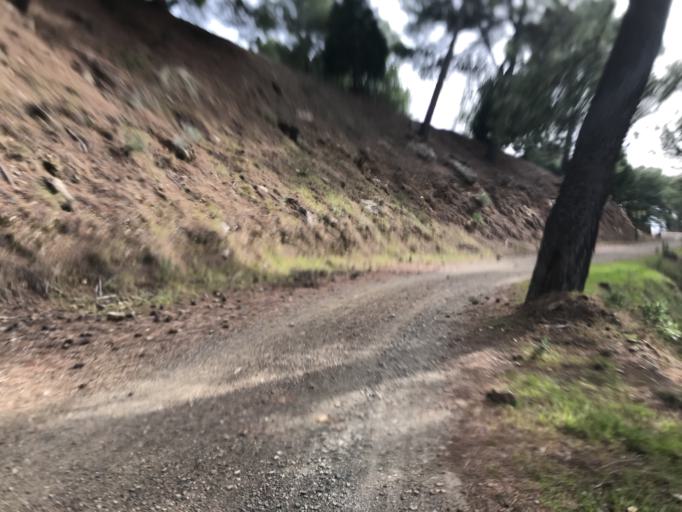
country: ES
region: Andalusia
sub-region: Provincia de Malaga
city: Malaga
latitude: 36.8003
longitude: -4.3992
